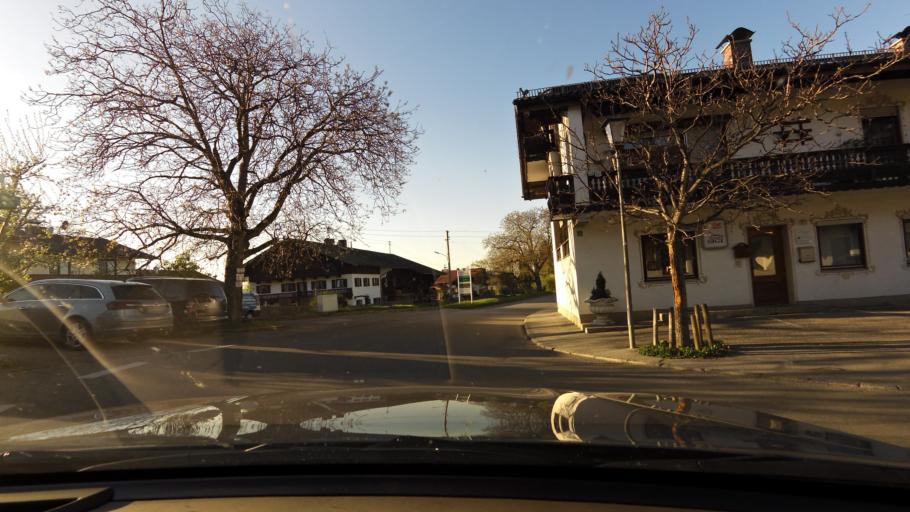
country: DE
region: Bavaria
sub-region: Upper Bavaria
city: Bad Feilnbach
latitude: 47.7750
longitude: 12.0027
